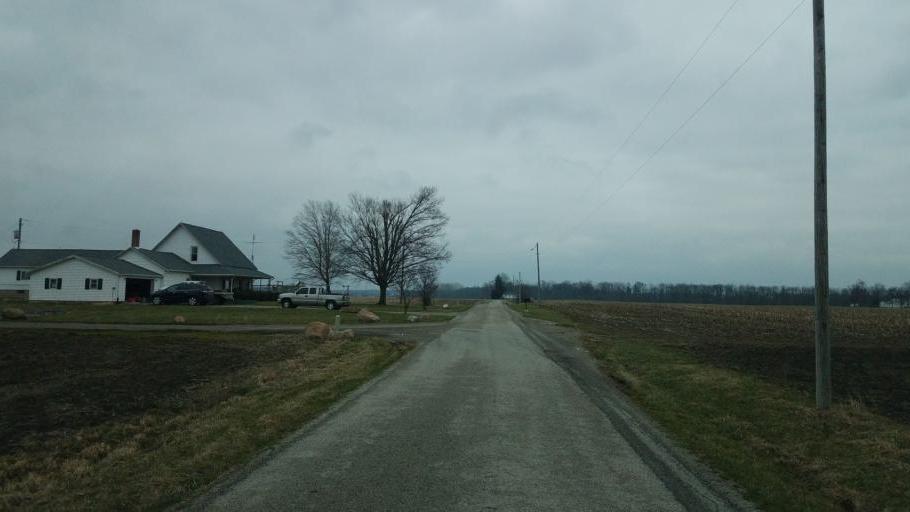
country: US
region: Ohio
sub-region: Morrow County
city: Cardington
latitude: 40.5142
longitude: -82.9537
